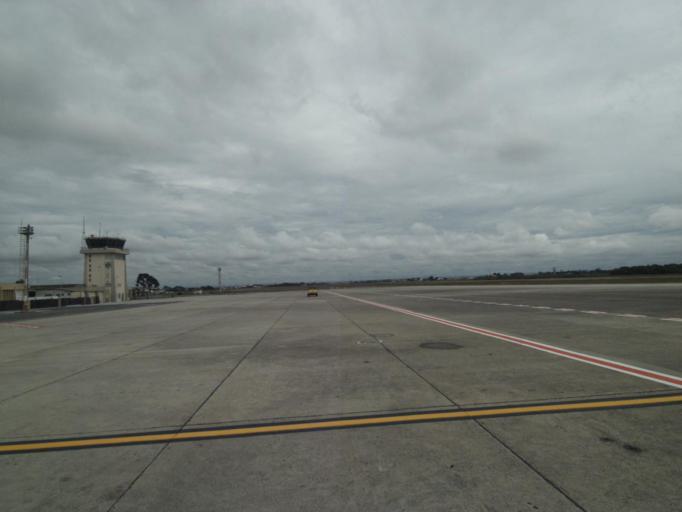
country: BR
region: Parana
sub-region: Sao Jose Dos Pinhais
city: Sao Jose dos Pinhais
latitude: -25.5321
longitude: -49.1745
